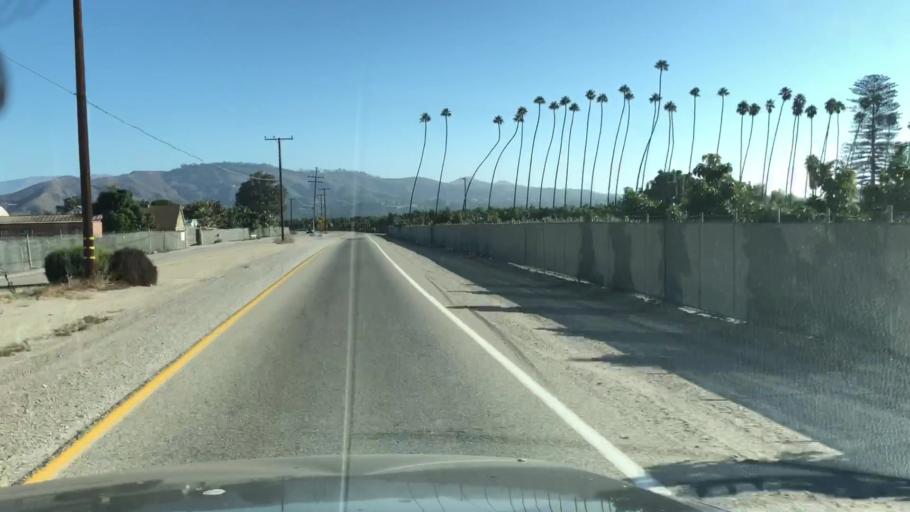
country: US
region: California
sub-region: Ventura County
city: Saticoy
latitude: 34.2621
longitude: -119.1300
